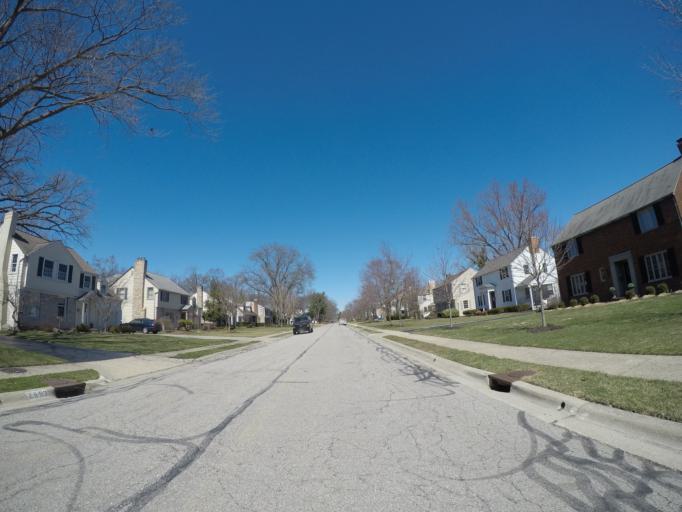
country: US
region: Ohio
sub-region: Franklin County
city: Upper Arlington
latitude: 40.0086
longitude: -83.0603
